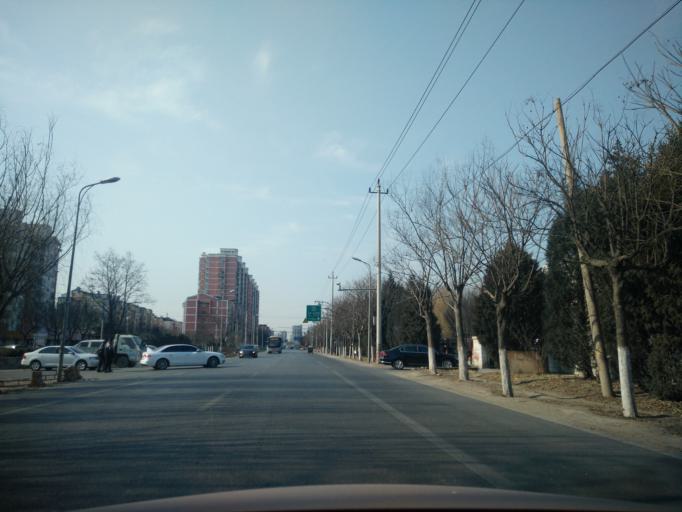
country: CN
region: Beijing
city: Yinghai
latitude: 39.7649
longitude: 116.4491
